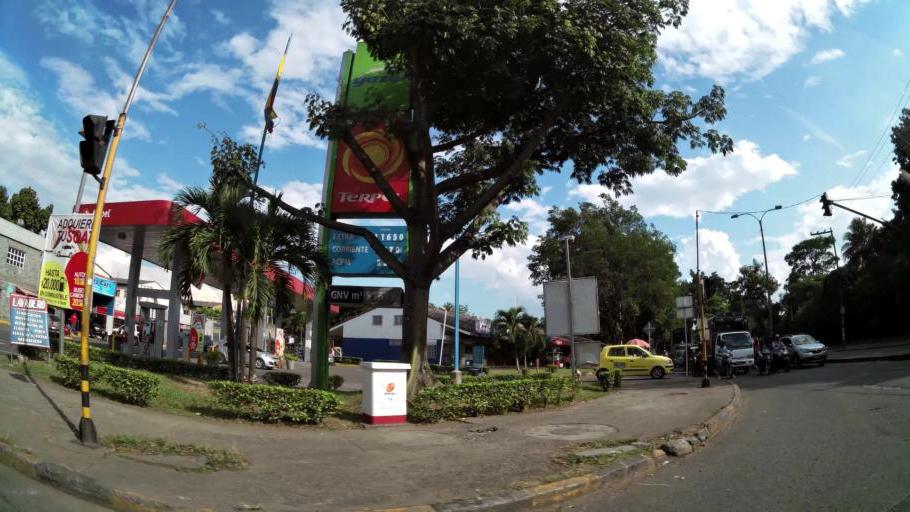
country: CO
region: Valle del Cauca
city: Cali
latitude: 3.4678
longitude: -76.5166
